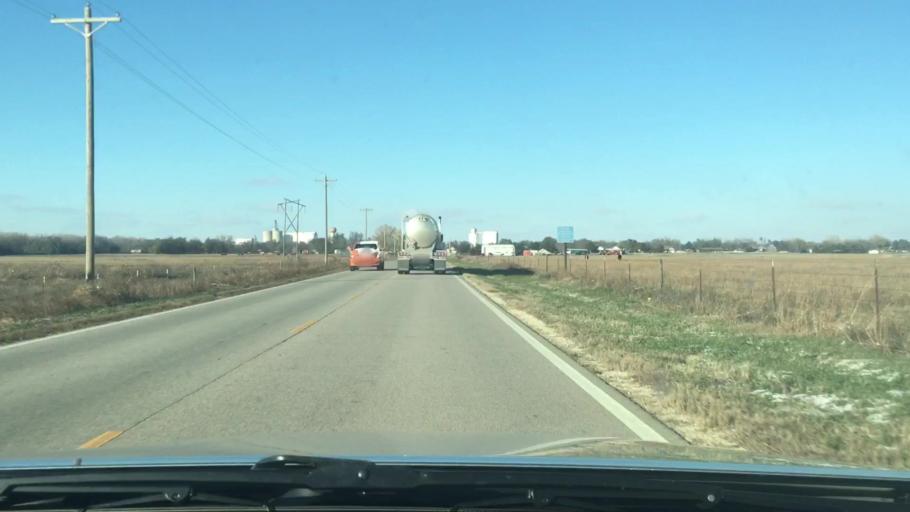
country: US
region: Kansas
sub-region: Rice County
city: Sterling
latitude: 38.1940
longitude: -98.2067
